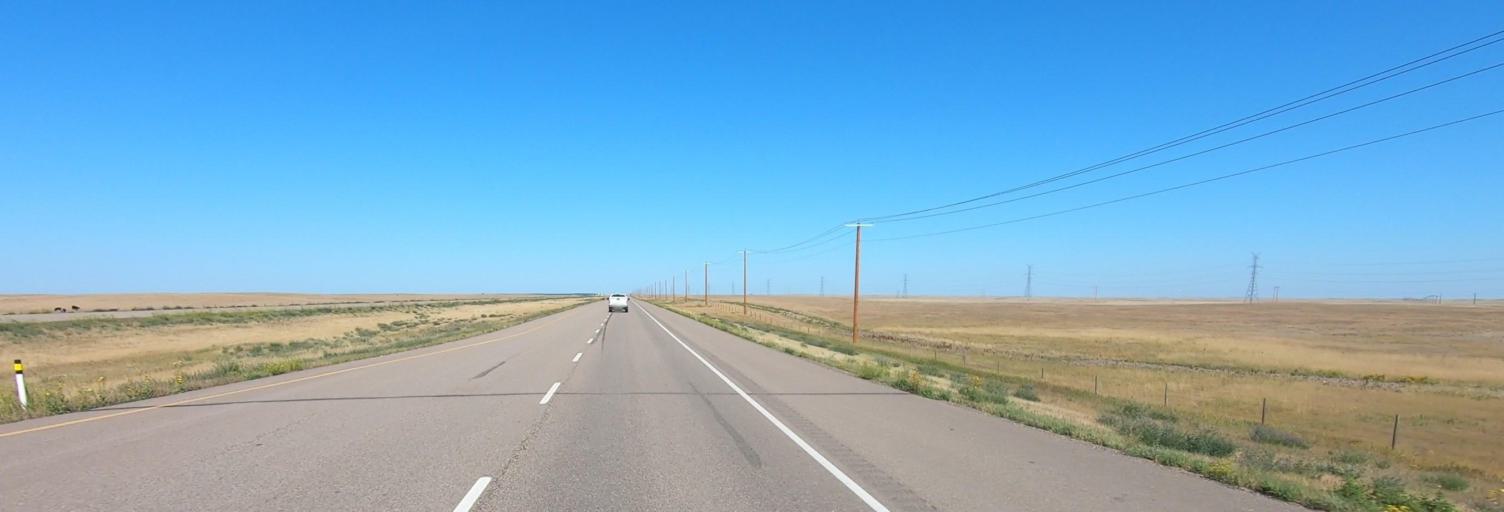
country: CA
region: Alberta
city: Bow Island
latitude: 50.2444
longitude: -111.2195
